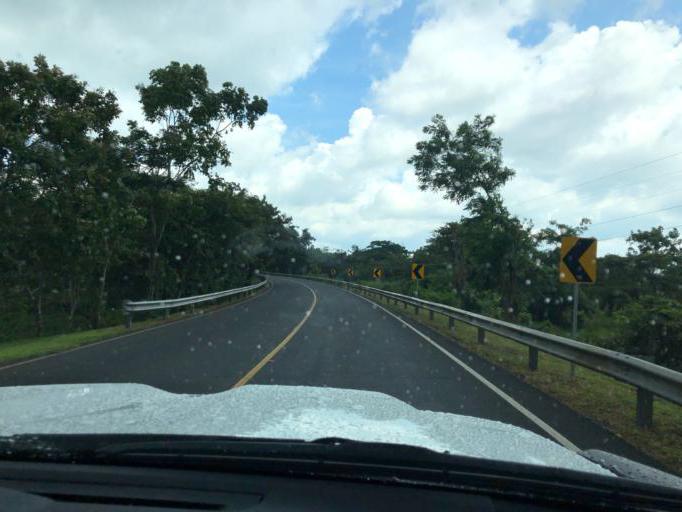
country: NI
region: Chontales
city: Villa Sandino
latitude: 12.0072
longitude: -84.9426
